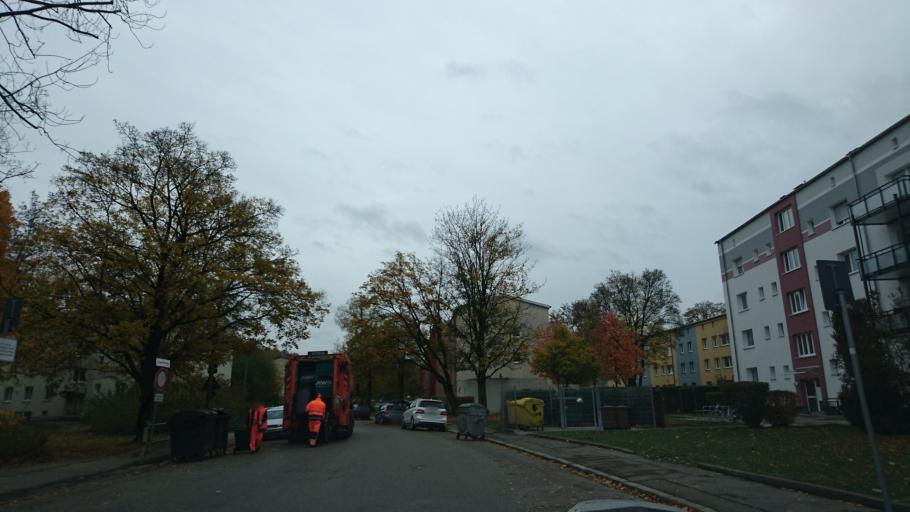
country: DE
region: Bavaria
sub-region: Swabia
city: Augsburg
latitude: 48.3572
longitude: 10.9299
